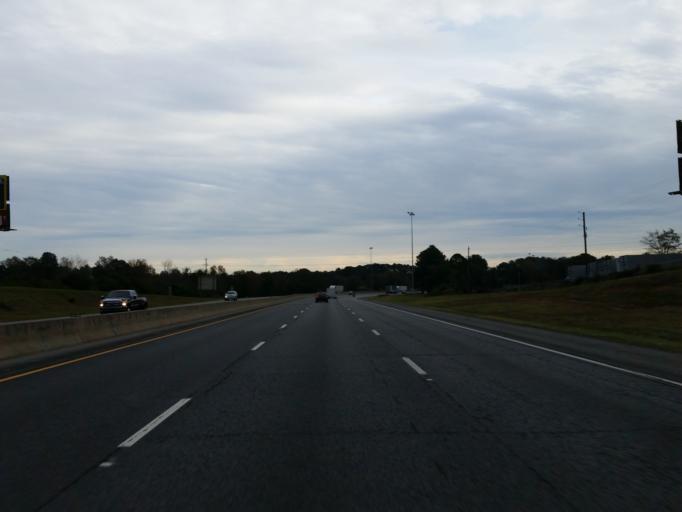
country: US
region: Georgia
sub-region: Tift County
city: Unionville
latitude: 31.4240
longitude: -83.5099
